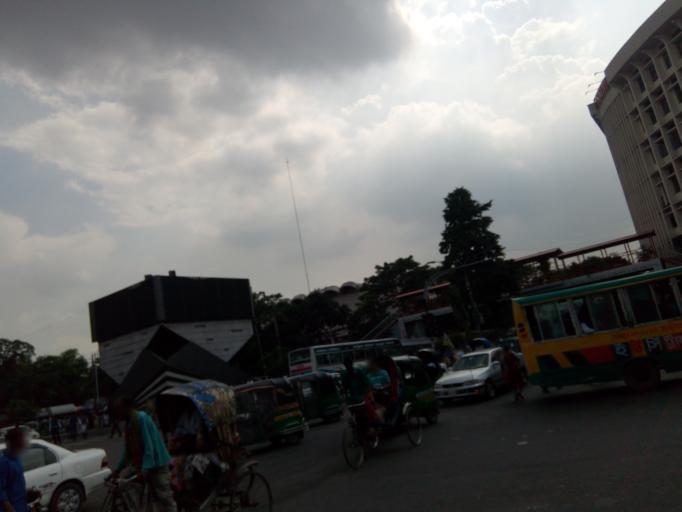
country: BD
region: Dhaka
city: Azimpur
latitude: 23.7383
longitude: 90.3960
